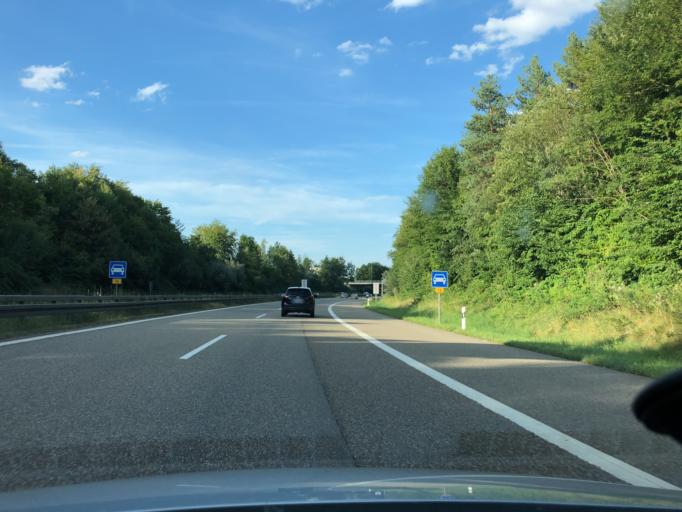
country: DE
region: Baden-Wuerttemberg
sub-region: Regierungsbezirk Stuttgart
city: Gerlingen
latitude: 48.7352
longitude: 9.0935
